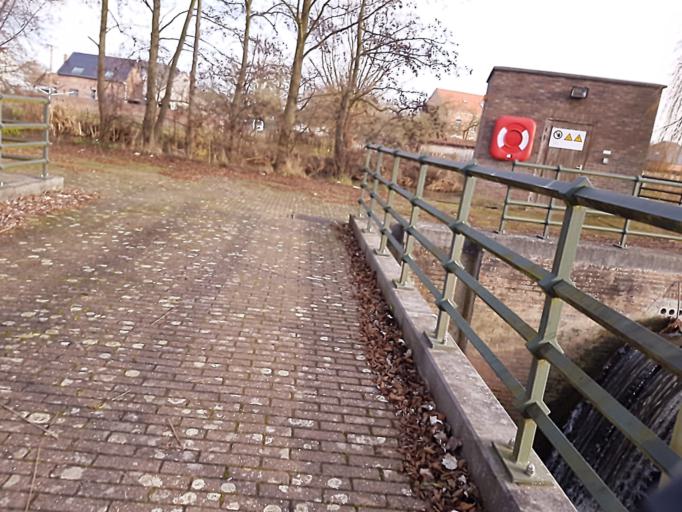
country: BE
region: Flanders
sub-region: Provincie Vlaams-Brabant
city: Rotselaar
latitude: 50.9466
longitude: 4.7022
